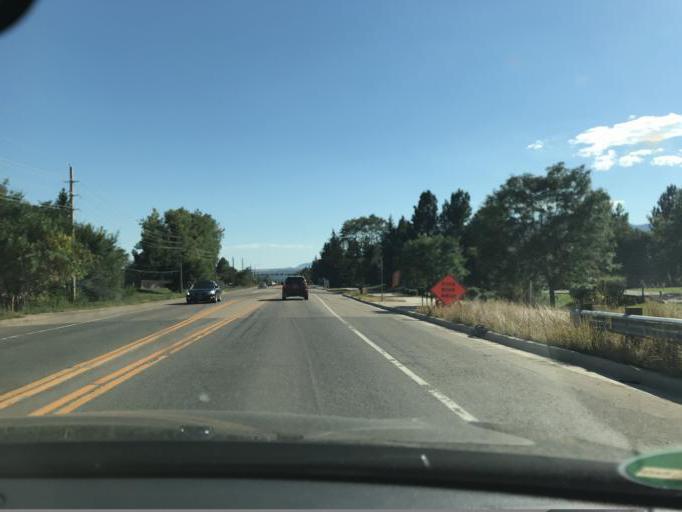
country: US
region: Colorado
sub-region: Boulder County
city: Boulder
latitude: 40.0463
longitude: -105.2586
